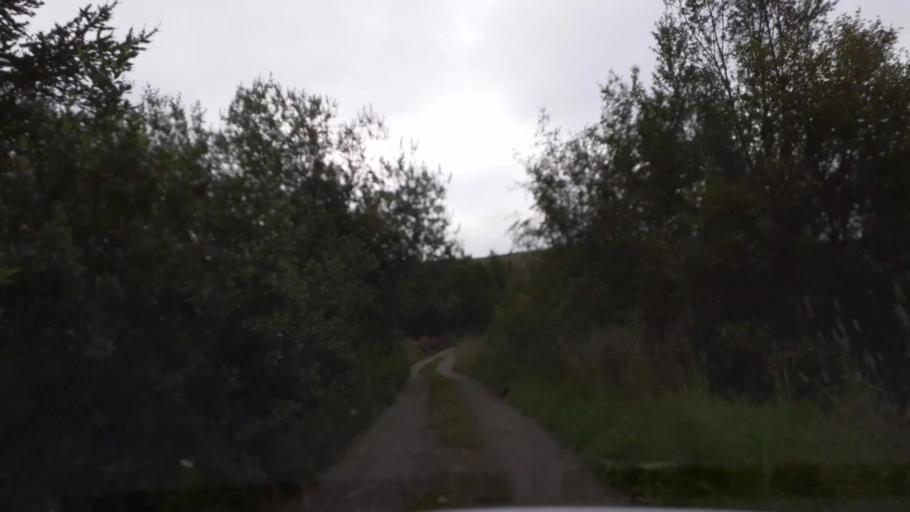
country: IS
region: Northeast
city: Akureyri
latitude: 65.6789
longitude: -18.0415
